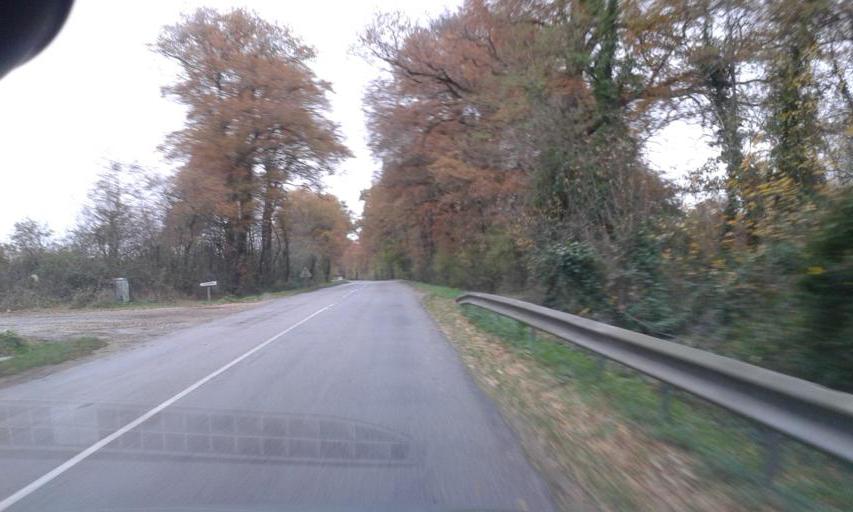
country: FR
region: Centre
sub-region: Departement du Loiret
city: Chateauneuf-sur-Loire
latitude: 47.8860
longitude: 2.2348
